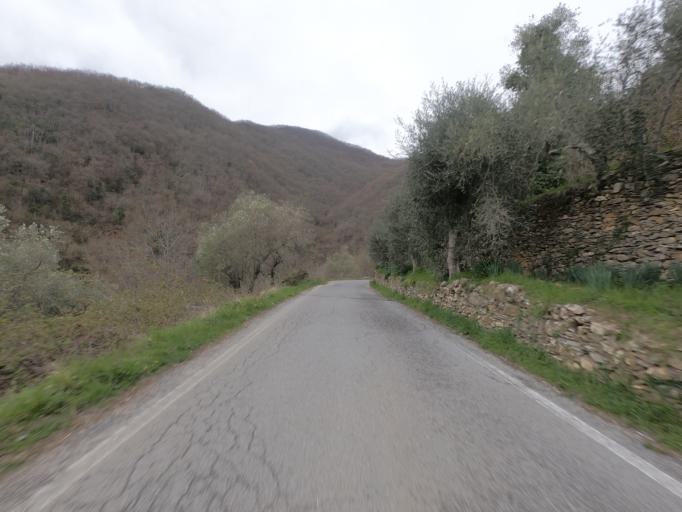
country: IT
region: Liguria
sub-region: Provincia di Savona
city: Testico
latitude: 44.0307
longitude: 8.0172
